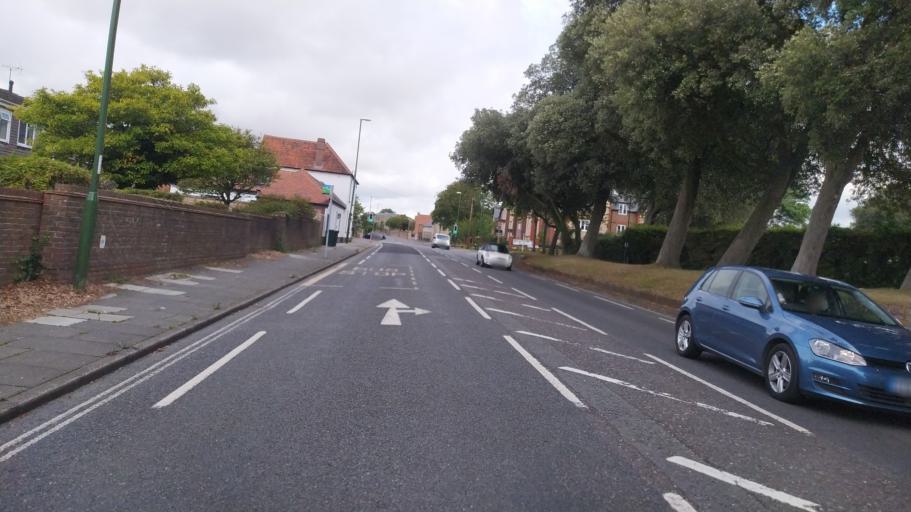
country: GB
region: England
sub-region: West Sussex
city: Chichester
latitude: 50.8471
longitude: -0.7794
